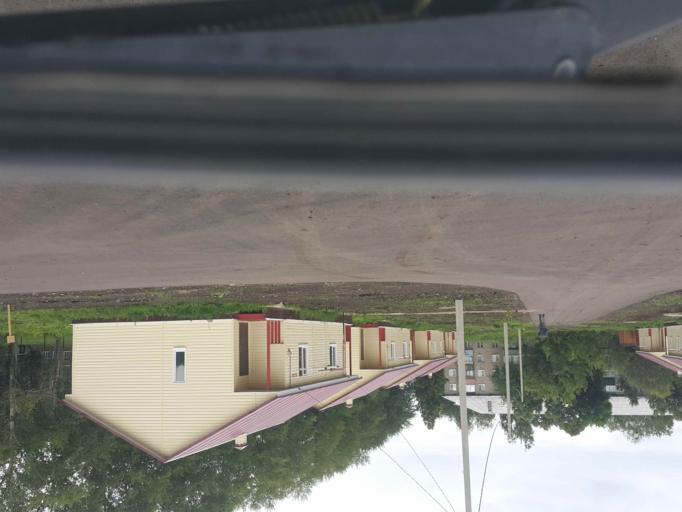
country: RU
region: Tambov
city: Michurinsk
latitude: 52.9516
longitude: 40.4916
